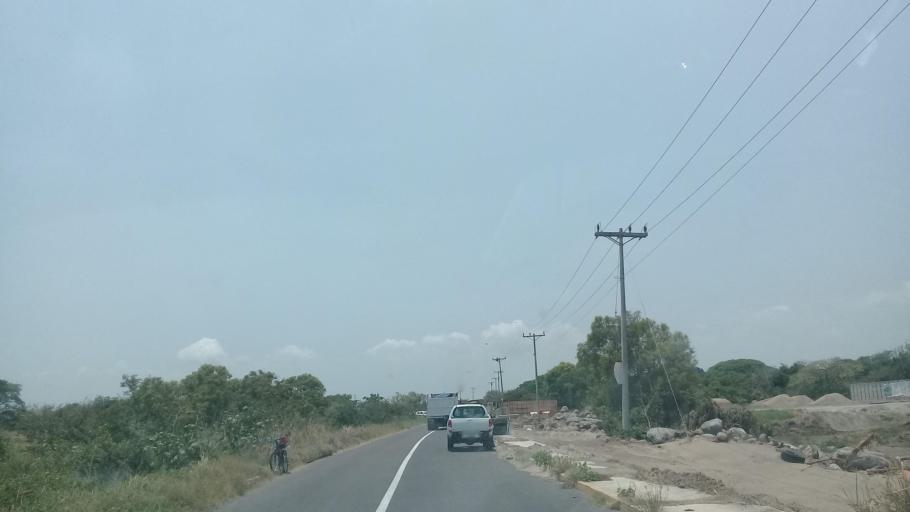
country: MX
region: Veracruz
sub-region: Veracruz
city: Hacienda Sotavento
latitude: 19.1436
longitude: -96.1724
